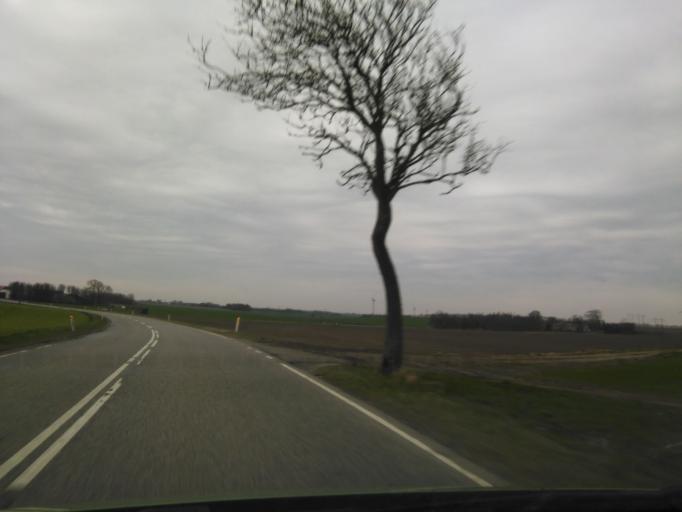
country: DK
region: Central Jutland
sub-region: Randers Kommune
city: Spentrup
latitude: 56.5859
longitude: 9.9949
